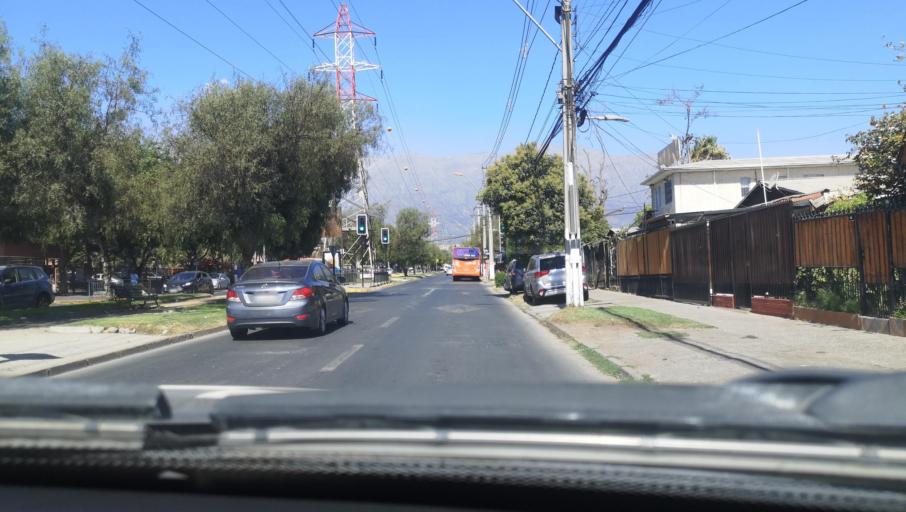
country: CL
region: Santiago Metropolitan
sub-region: Provincia de Santiago
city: Villa Presidente Frei, Nunoa, Santiago, Chile
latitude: -33.5016
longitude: -70.5806
